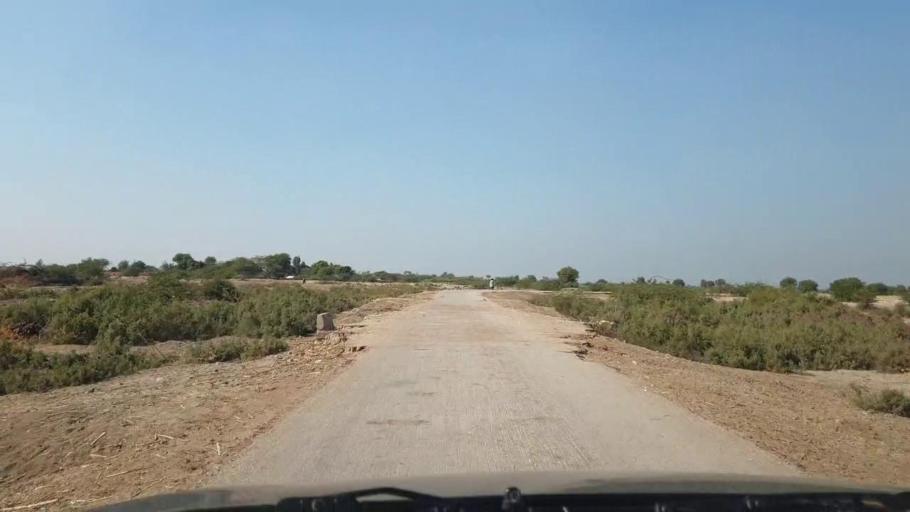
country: PK
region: Sindh
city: Jhol
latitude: 25.9085
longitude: 68.8283
